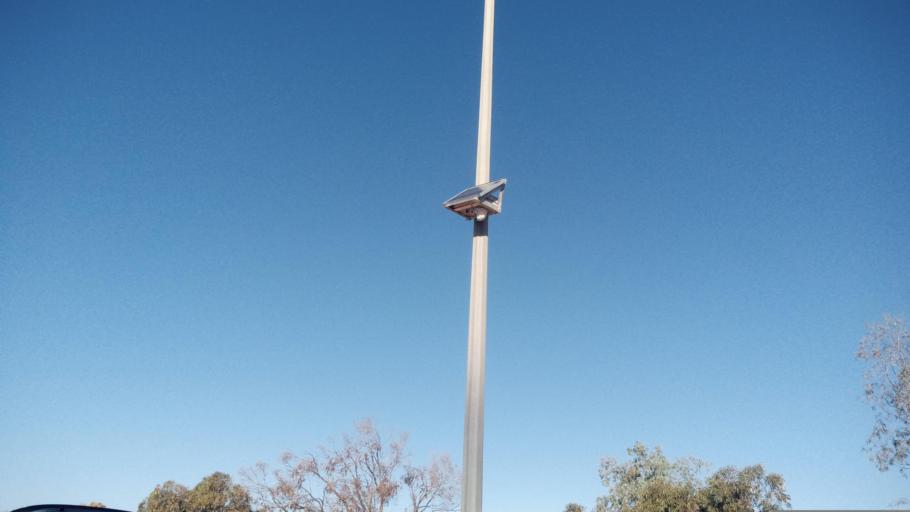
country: TN
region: Madanin
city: Bin Qirdan
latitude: 33.1529
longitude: 11.3081
